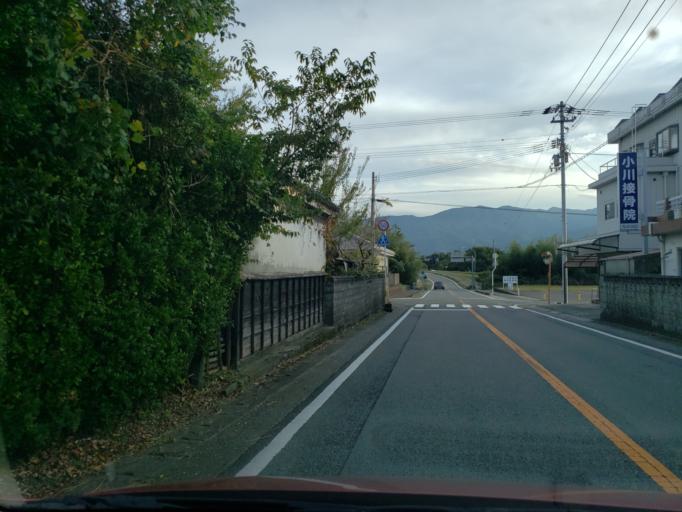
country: JP
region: Tokushima
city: Wakimachi
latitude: 34.0745
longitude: 134.2365
